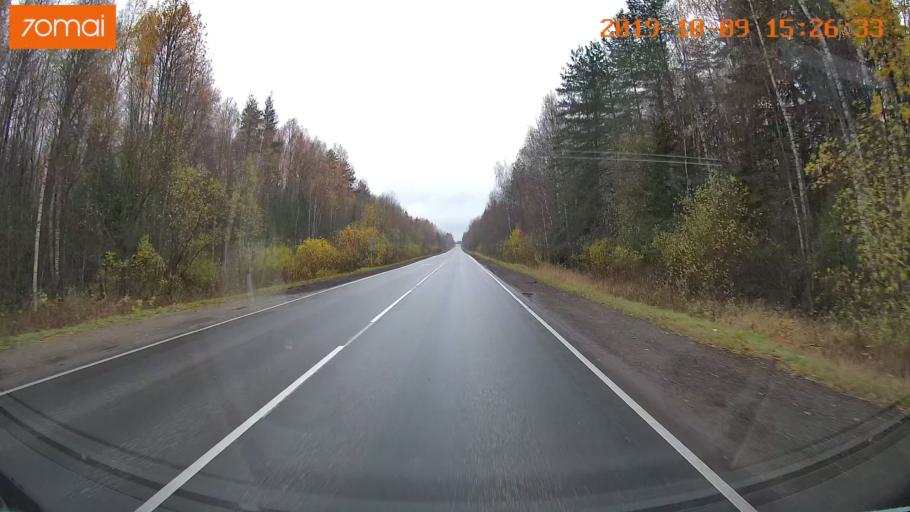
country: RU
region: Kostroma
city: Susanino
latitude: 58.0193
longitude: 41.4011
